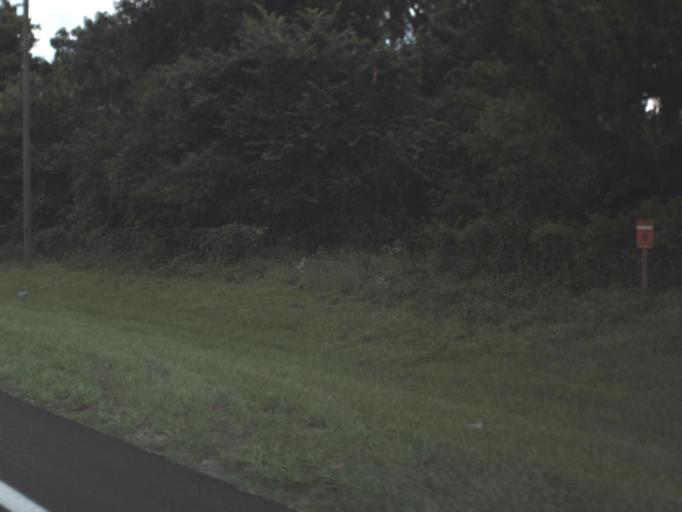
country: US
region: Florida
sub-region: Alachua County
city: Alachua
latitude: 29.7692
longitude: -82.4234
